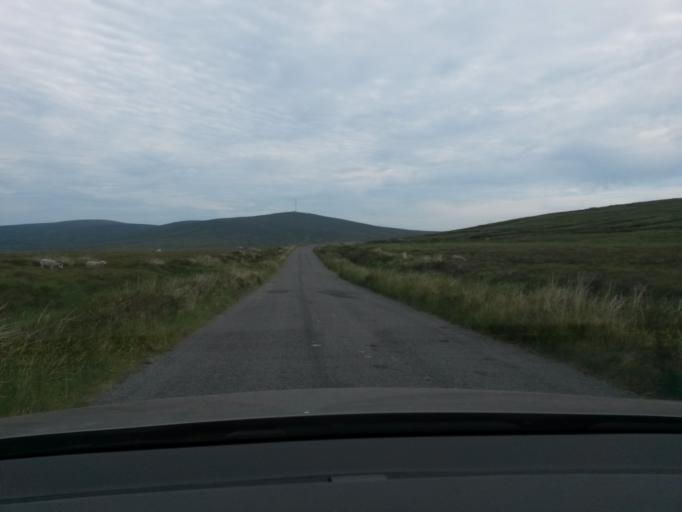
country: IE
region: Leinster
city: Ballyboden
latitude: 53.1387
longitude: -6.3124
